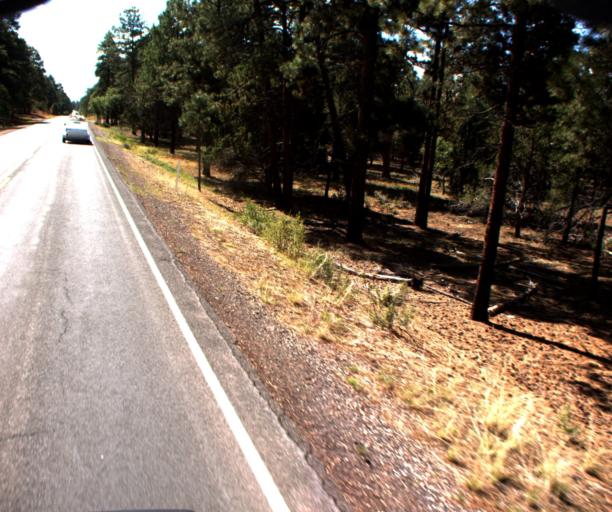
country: US
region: Arizona
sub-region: Coconino County
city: Grand Canyon
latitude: 36.0439
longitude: -112.0821
